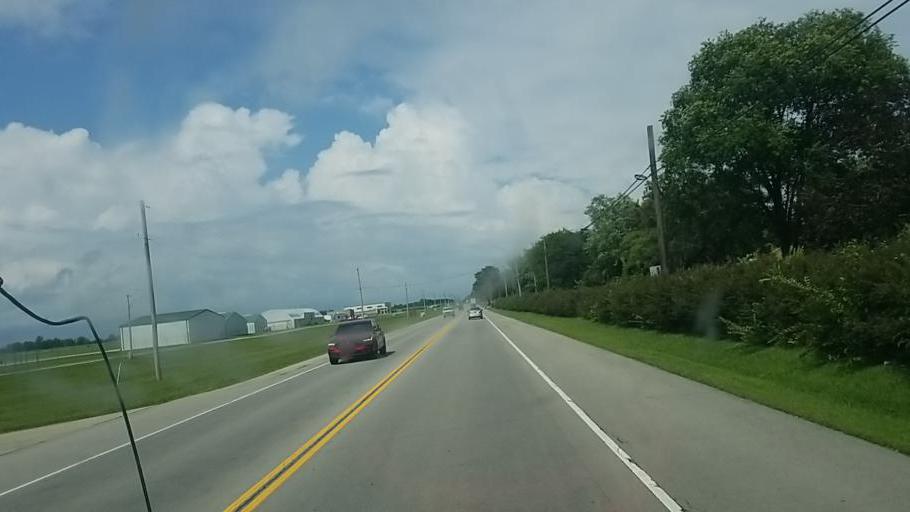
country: US
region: Ohio
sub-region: Champaign County
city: Urbana
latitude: 40.1289
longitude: -83.7485
